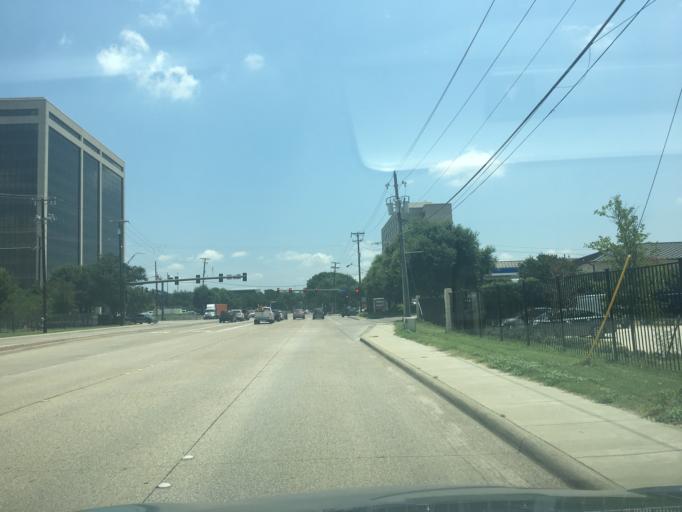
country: US
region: Texas
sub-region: Dallas County
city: Addison
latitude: 32.9398
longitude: -96.8404
